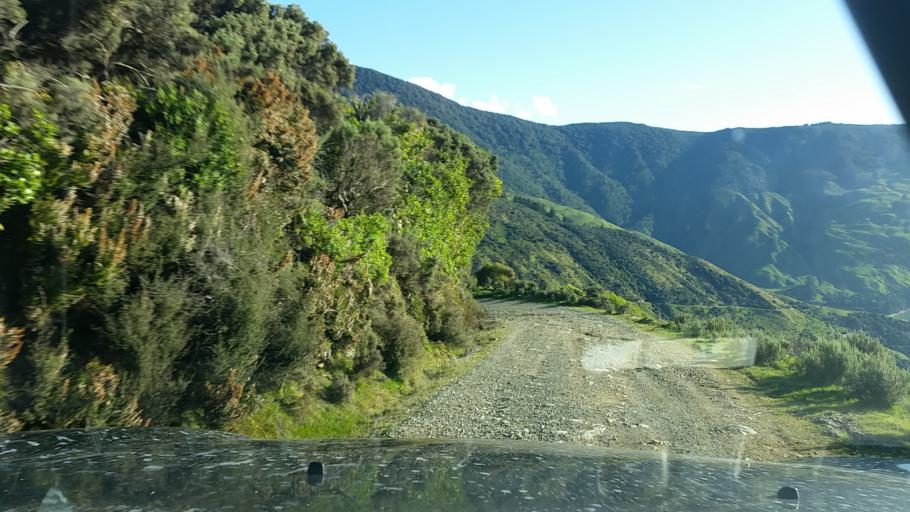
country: NZ
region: Marlborough
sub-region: Marlborough District
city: Picton
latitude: -41.0223
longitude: 174.1589
